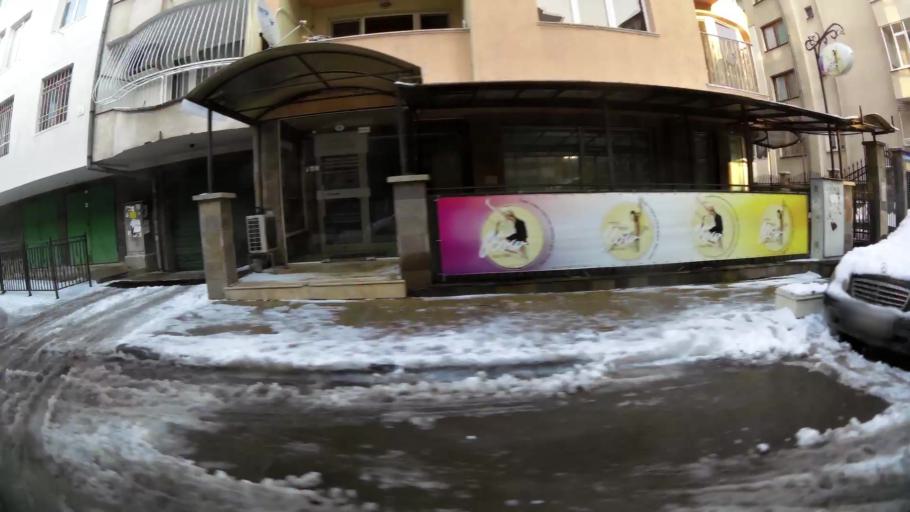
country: BG
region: Sofia-Capital
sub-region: Stolichna Obshtina
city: Sofia
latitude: 42.6887
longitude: 23.3661
